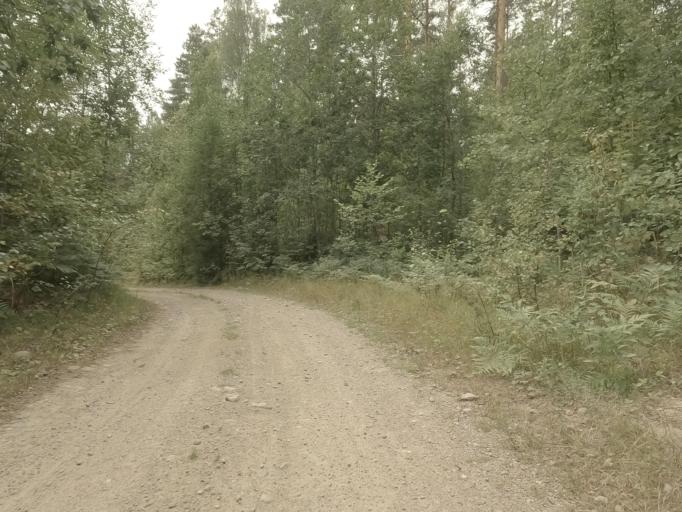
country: RU
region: Leningrad
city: Kamennogorsk
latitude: 61.0062
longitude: 29.1832
